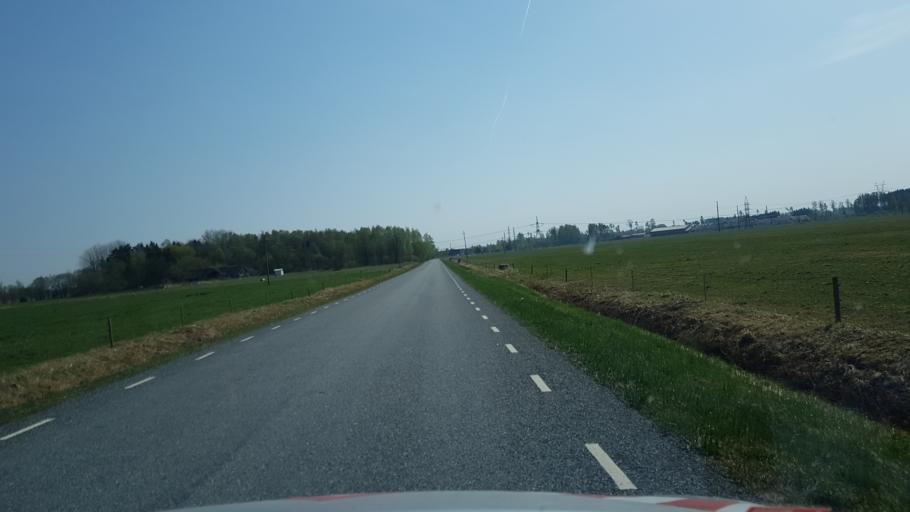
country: EE
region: Paernumaa
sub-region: Sindi linn
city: Sindi
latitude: 58.4332
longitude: 24.6280
